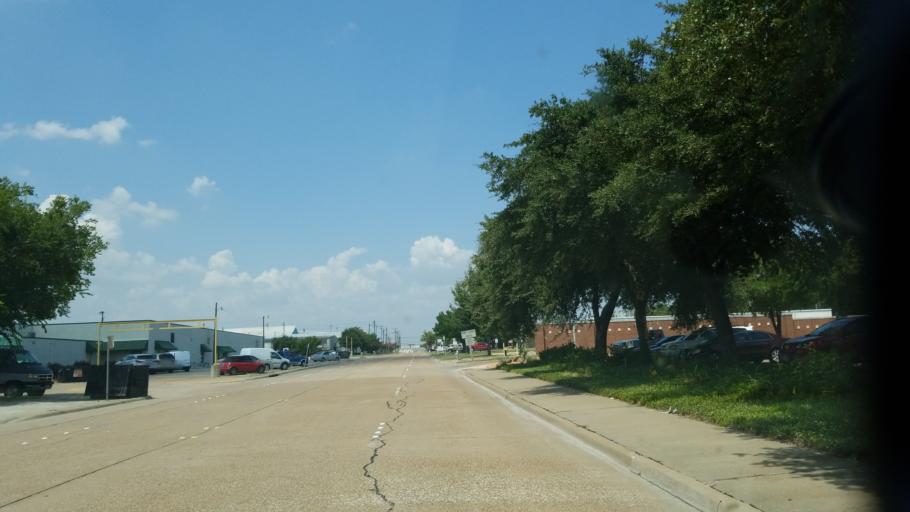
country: US
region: Texas
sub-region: Dallas County
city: Garland
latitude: 32.9183
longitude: -96.6361
